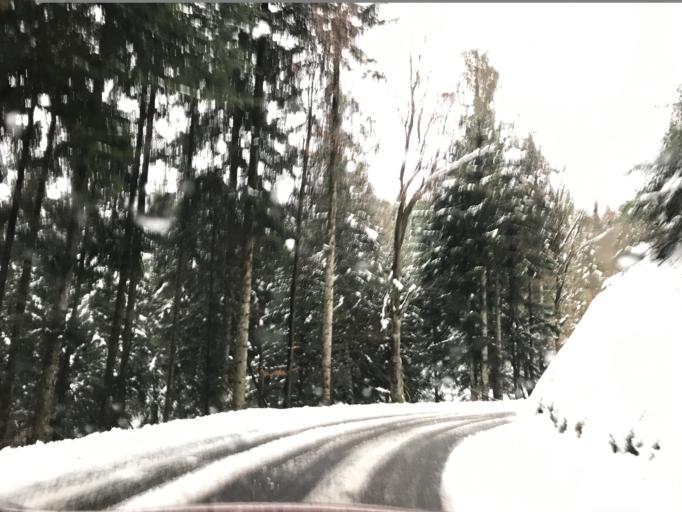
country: FR
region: Rhone-Alpes
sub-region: Departement de la Loire
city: Noiretable
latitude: 45.7494
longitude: 3.6715
